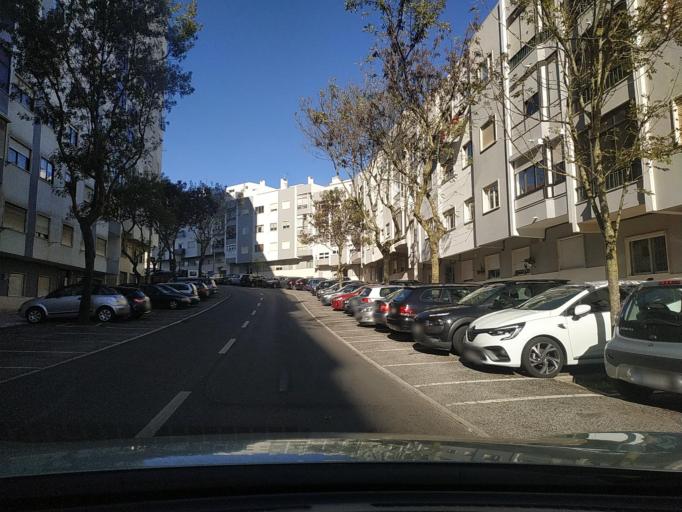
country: PT
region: Lisbon
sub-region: Amadora
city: Amadora
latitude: 38.7691
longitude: -9.2258
